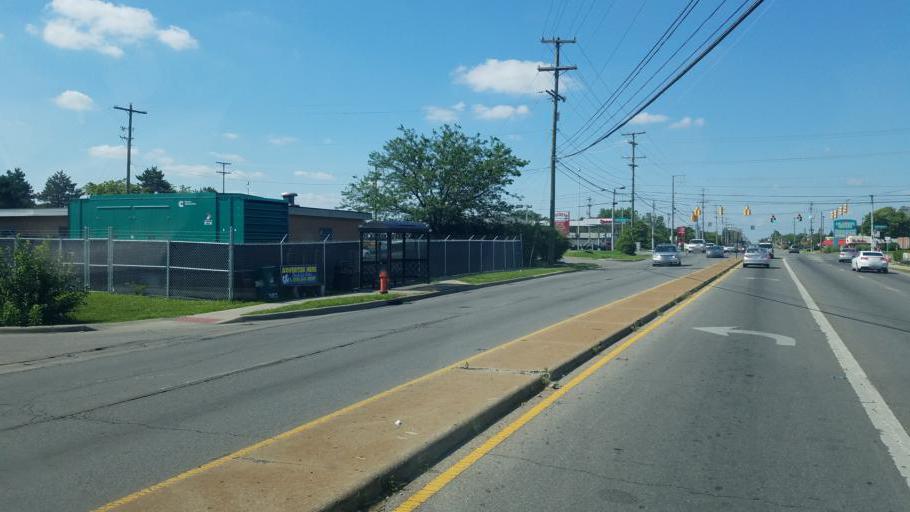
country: US
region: Ohio
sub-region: Franklin County
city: Minerva Park
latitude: 40.0840
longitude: -82.9511
